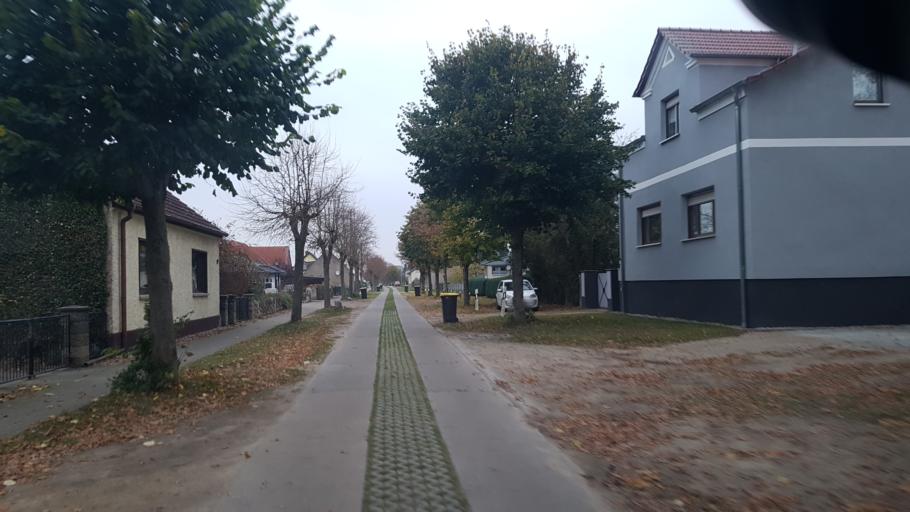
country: DE
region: Brandenburg
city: Ruthnick
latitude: 52.8980
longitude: 12.9704
